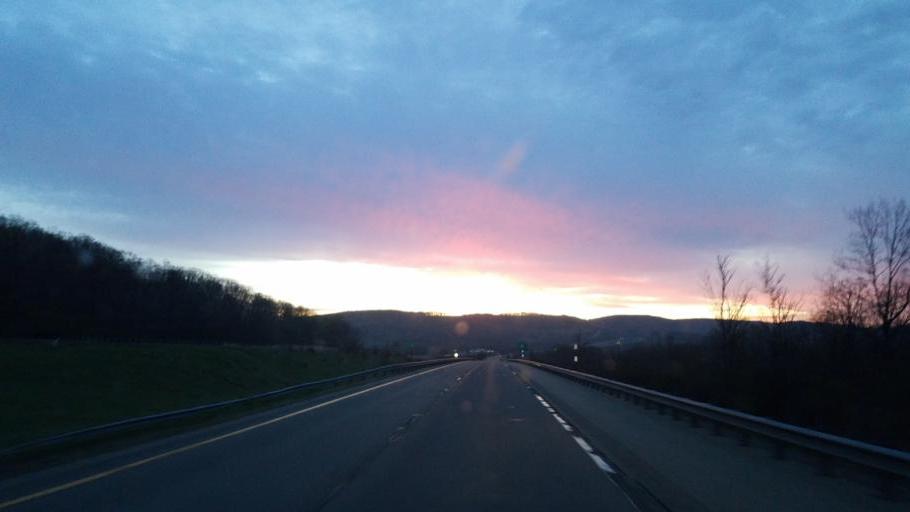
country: US
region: New York
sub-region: Allegany County
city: Cuba
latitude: 42.2209
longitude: -78.2908
